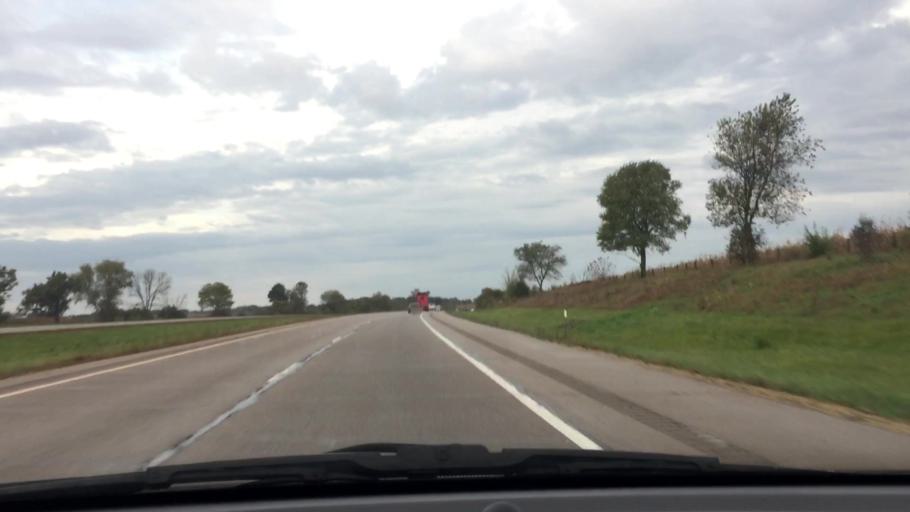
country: US
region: Wisconsin
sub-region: Rock County
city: Clinton
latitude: 42.5723
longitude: -88.8120
